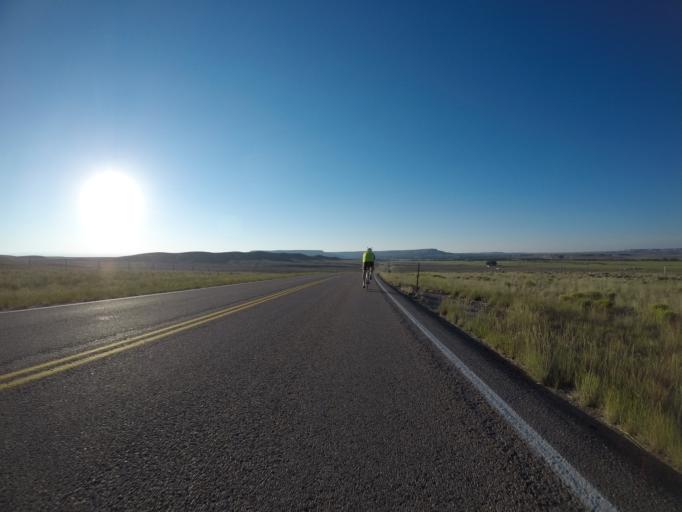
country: US
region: Wyoming
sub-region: Sublette County
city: Marbleton
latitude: 42.5800
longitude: -109.9914
